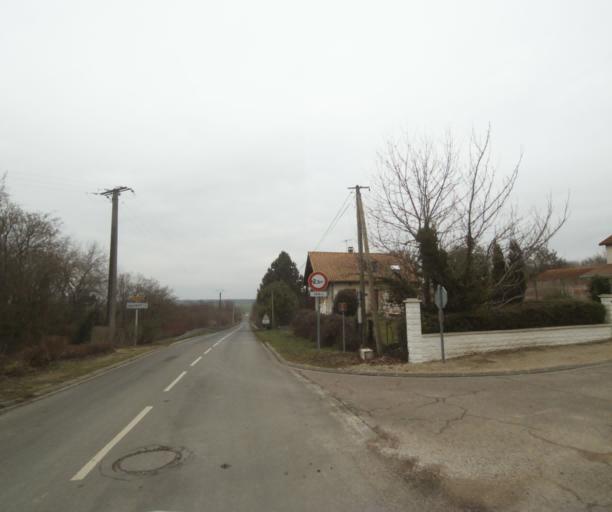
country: FR
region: Champagne-Ardenne
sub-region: Departement de la Haute-Marne
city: Villiers-en-Lieu
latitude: 48.6391
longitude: 4.7678
